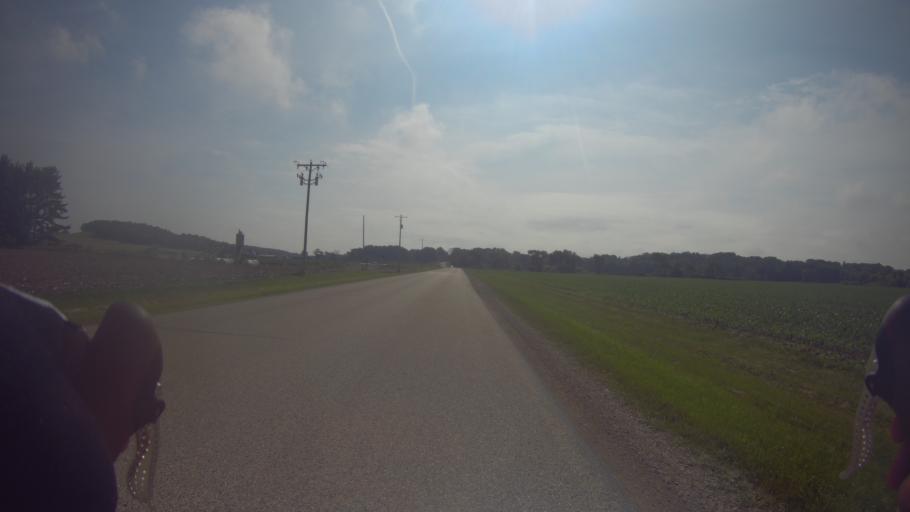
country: US
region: Wisconsin
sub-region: Dane County
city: Stoughton
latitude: 42.9918
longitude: -89.1985
